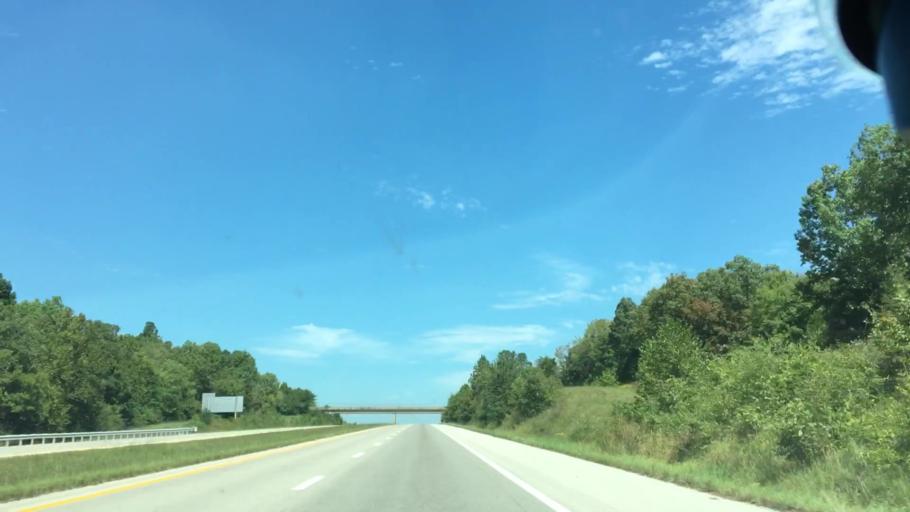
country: US
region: Kentucky
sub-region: Christian County
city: Hopkinsville
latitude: 36.9207
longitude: -87.4733
